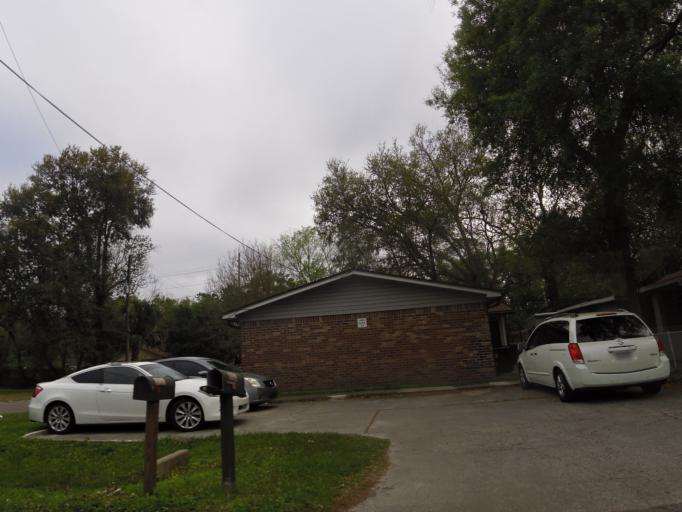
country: US
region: Florida
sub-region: Duval County
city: Jacksonville
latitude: 30.3233
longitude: -81.7157
